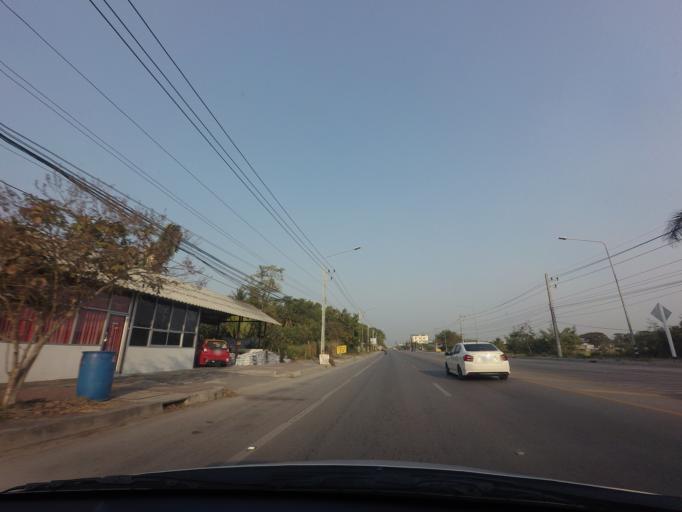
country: TH
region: Nakhon Pathom
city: Nakhon Chai Si
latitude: 13.8047
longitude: 100.2263
